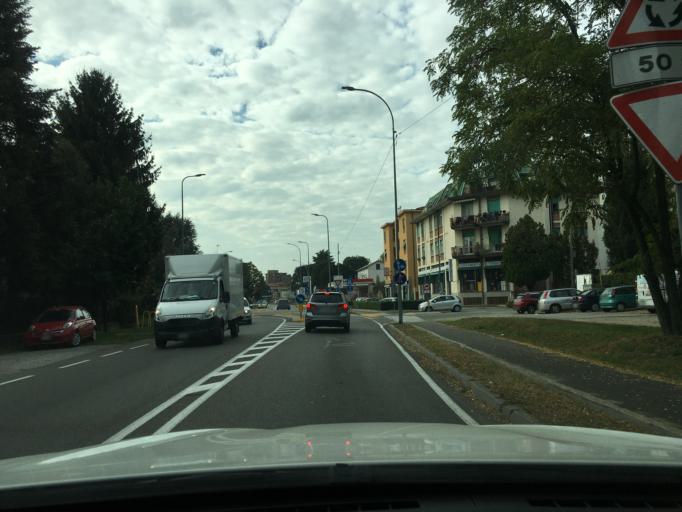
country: IT
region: Lombardy
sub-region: Provincia di Monza e Brianza
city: Muggio
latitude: 45.5925
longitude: 9.2376
